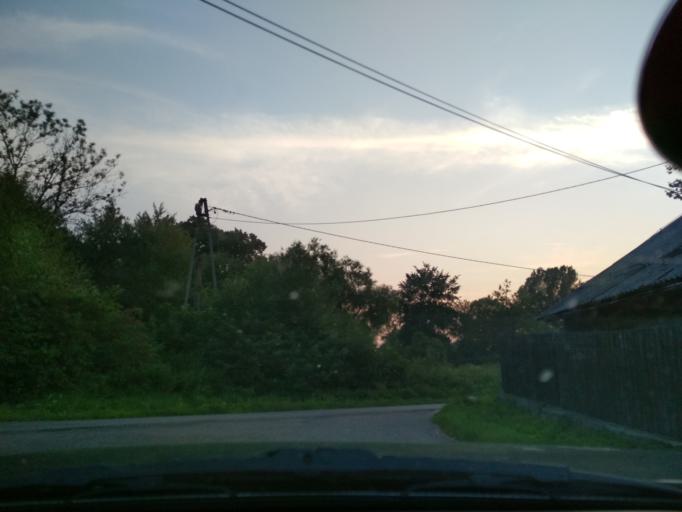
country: PL
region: Lesser Poland Voivodeship
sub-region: Powiat olkuski
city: Wolbrom
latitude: 50.4571
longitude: 19.7889
